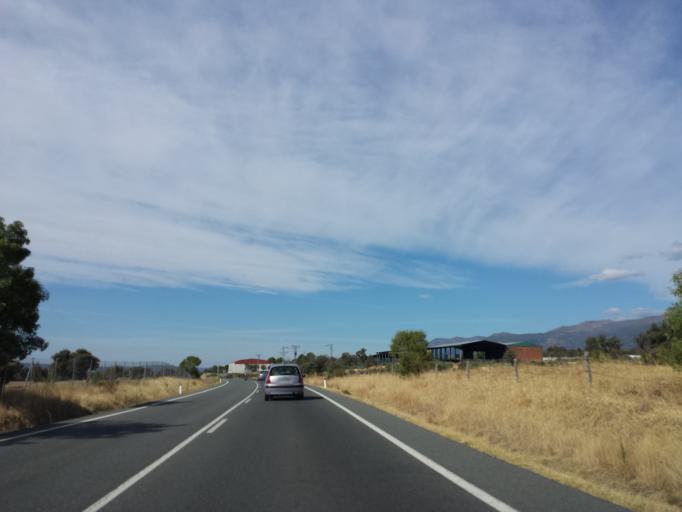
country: ES
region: Castille and Leon
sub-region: Provincia de Avila
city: Casavieja
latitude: 40.2740
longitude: -4.7439
